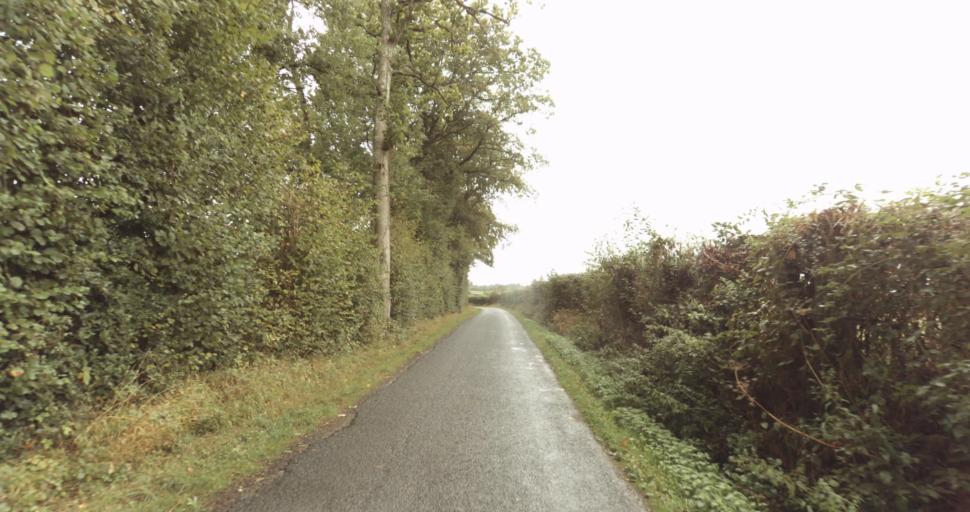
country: FR
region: Lower Normandy
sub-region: Departement de l'Orne
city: Sainte-Gauburge-Sainte-Colombe
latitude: 48.6891
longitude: 0.4348
